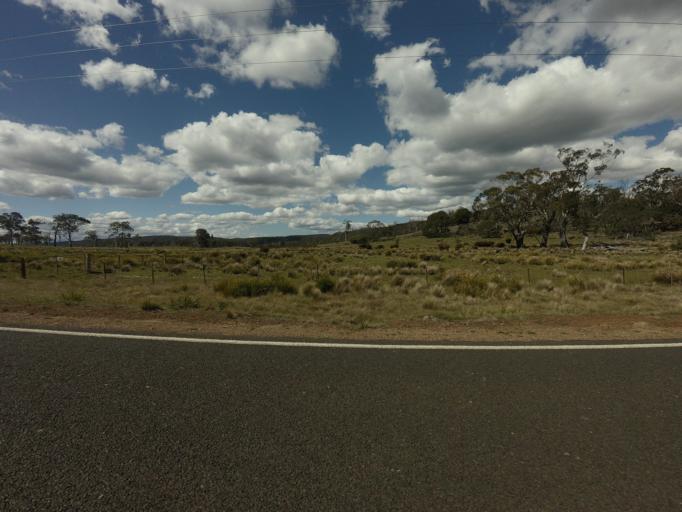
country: AU
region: Tasmania
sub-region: Northern Midlands
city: Evandale
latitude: -41.9498
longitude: 147.6071
